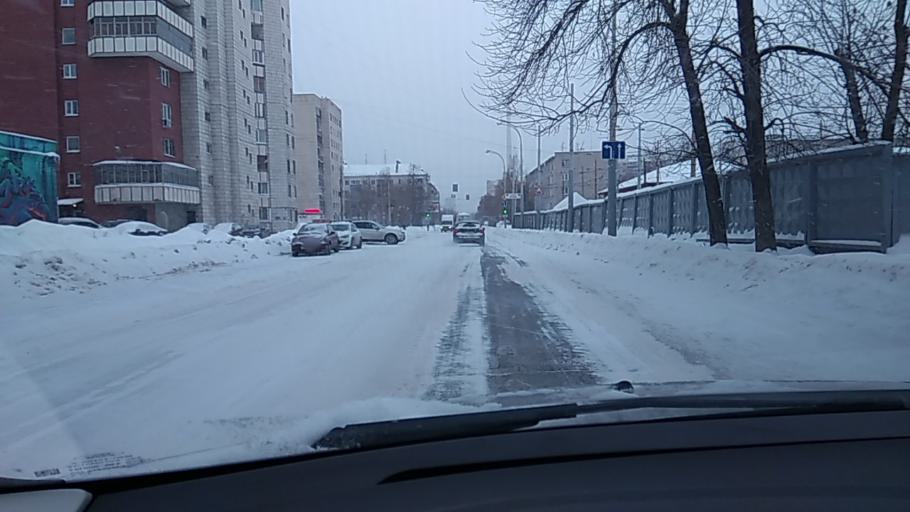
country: RU
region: Sverdlovsk
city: Yekaterinburg
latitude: 56.8124
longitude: 60.6118
